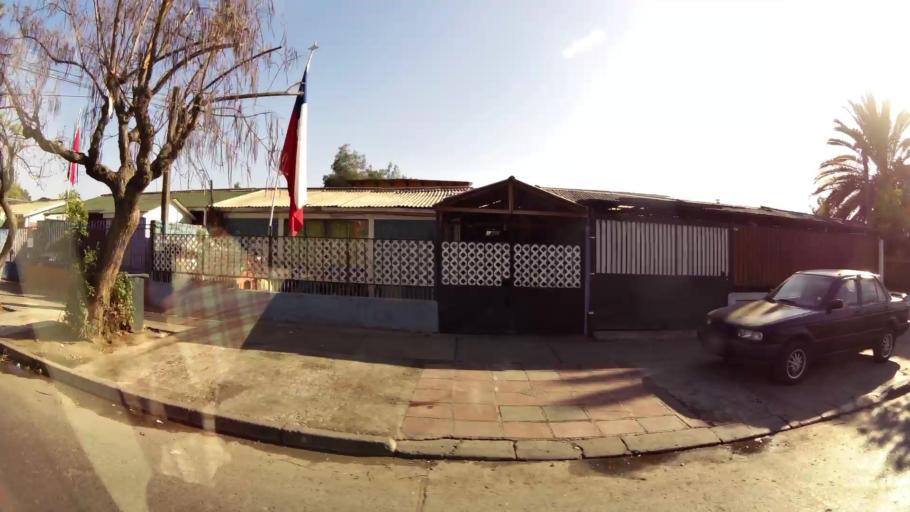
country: CL
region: Santiago Metropolitan
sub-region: Provincia de Santiago
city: Santiago
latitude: -33.3846
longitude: -70.6505
